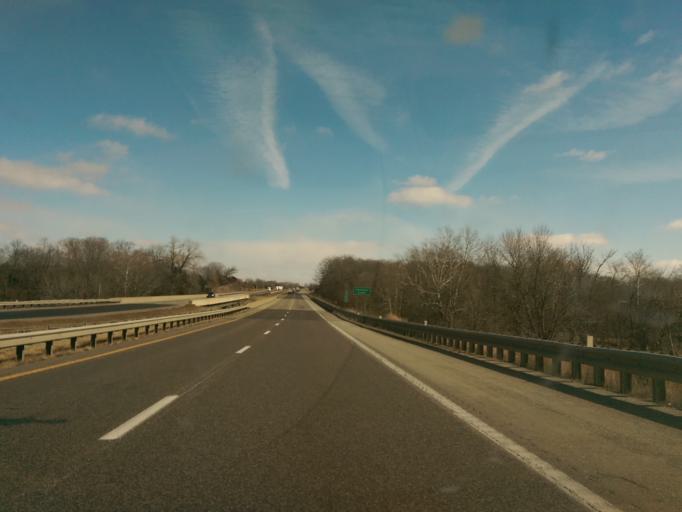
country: US
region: Missouri
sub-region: Callaway County
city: Fulton
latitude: 38.9358
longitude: -91.8454
